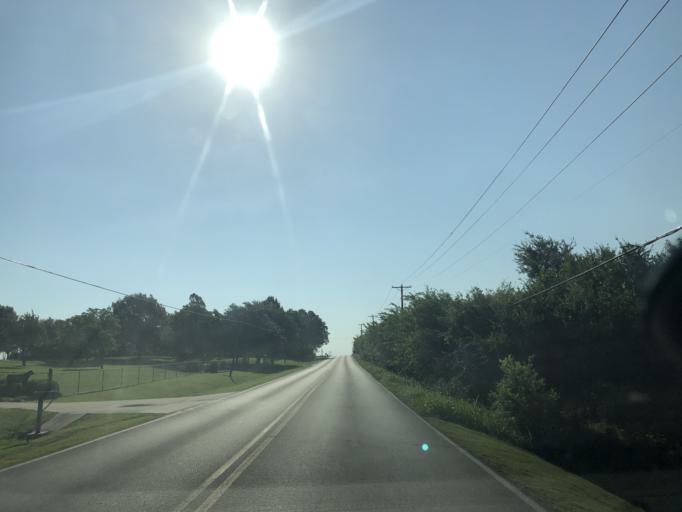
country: US
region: Texas
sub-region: Dallas County
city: Sunnyvale
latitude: 32.8139
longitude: -96.5660
